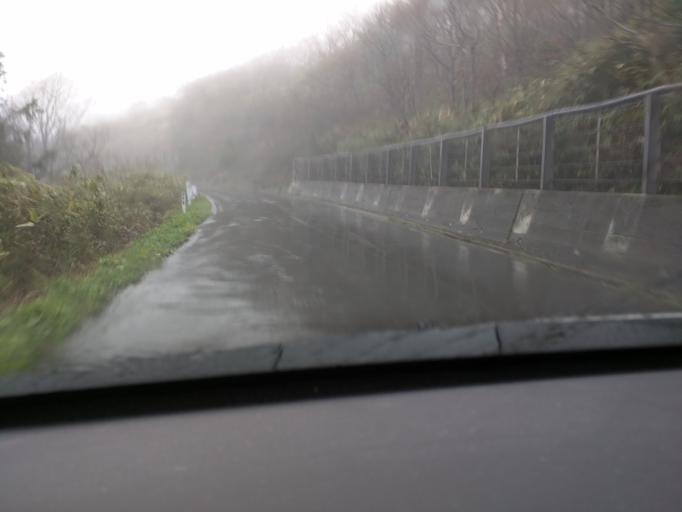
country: JP
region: Fukushima
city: Inawashiro
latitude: 37.6667
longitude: 140.2562
